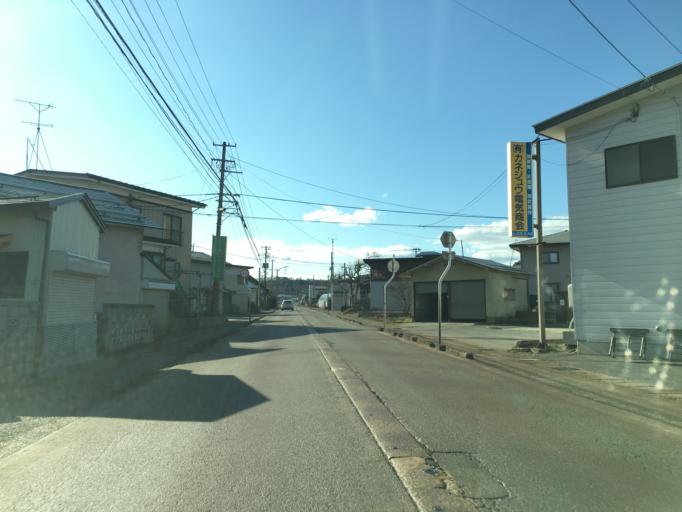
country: JP
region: Yamagata
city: Nagai
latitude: 38.0055
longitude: 140.0360
